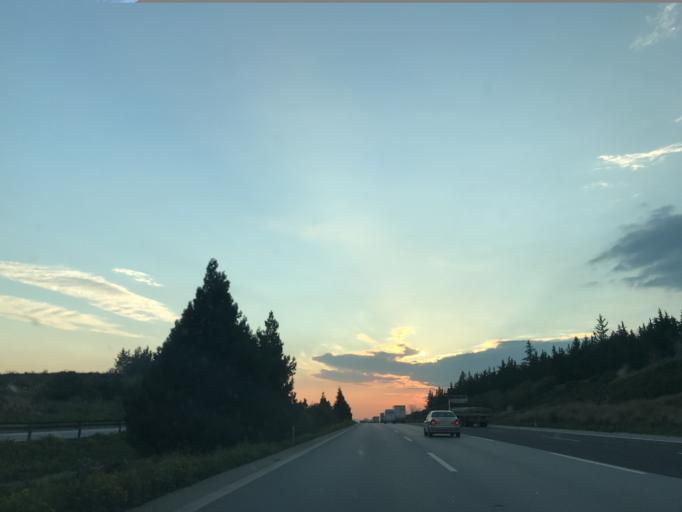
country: TR
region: Mersin
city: Yenice
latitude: 37.0177
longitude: 35.0059
